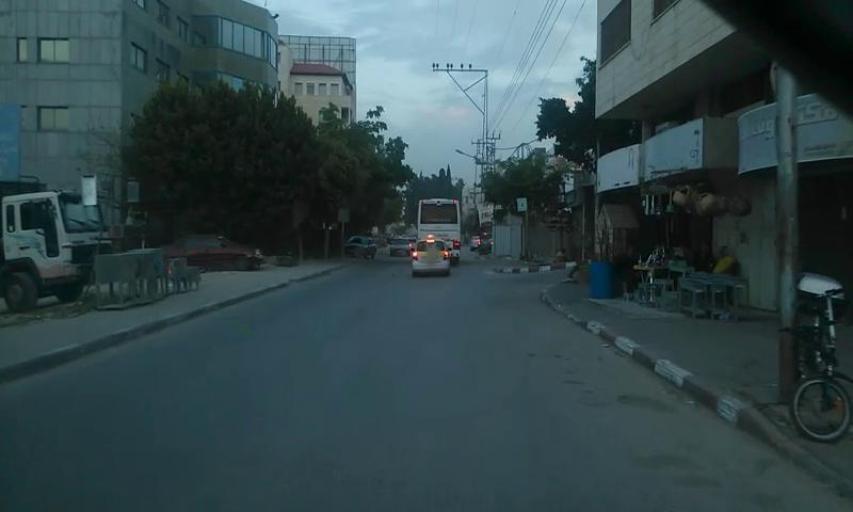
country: PS
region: West Bank
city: Tulkarm
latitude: 32.3174
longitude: 35.0314
